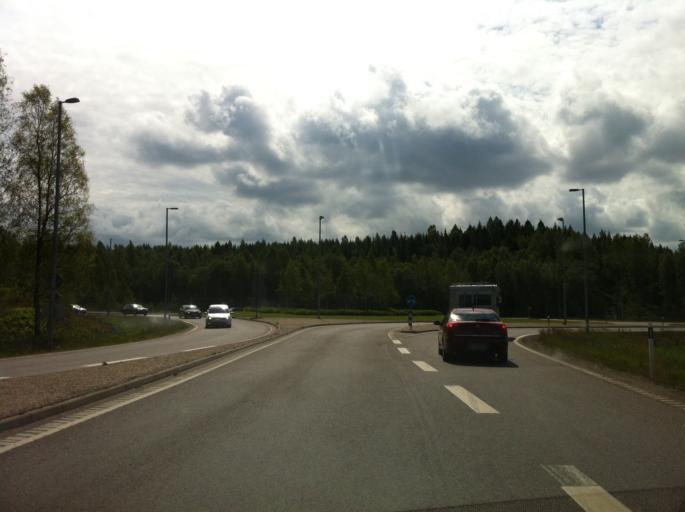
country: SE
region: Vaermland
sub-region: Karlstads Kommun
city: Valberg
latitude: 59.3690
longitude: 13.1441
